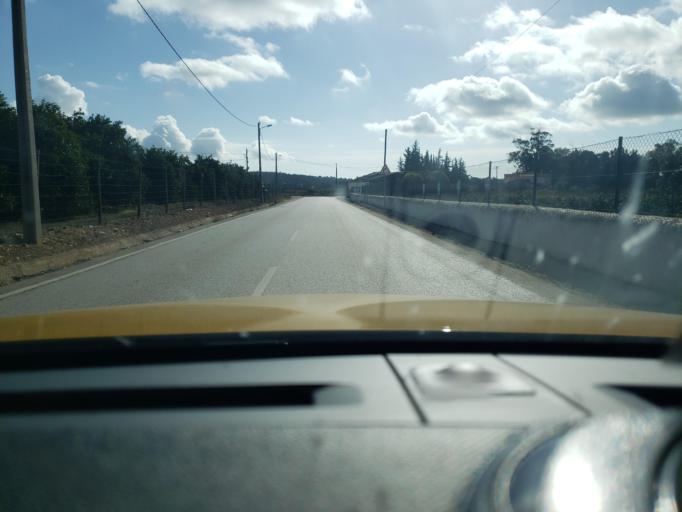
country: PT
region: Faro
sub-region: Portimao
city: Alvor
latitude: 37.1677
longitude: -8.5785
